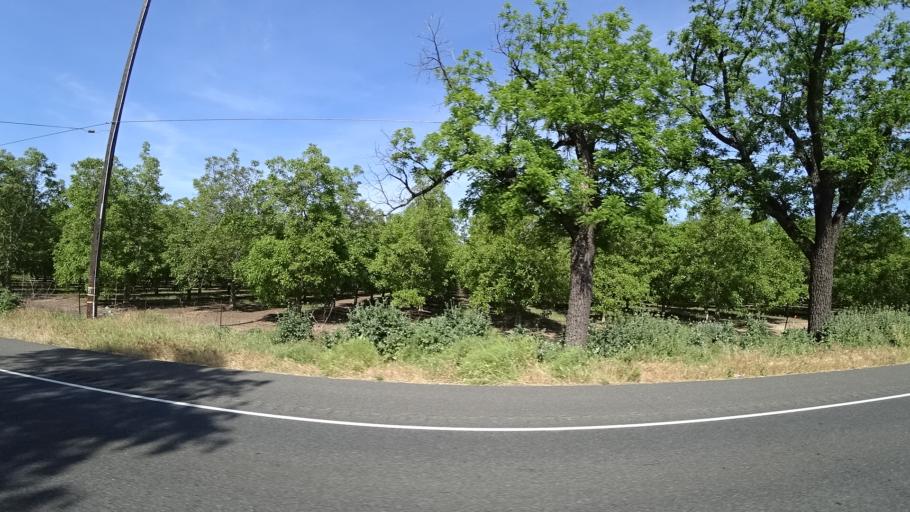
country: US
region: California
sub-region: Tehama County
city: Red Bluff
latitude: 40.1756
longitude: -122.1679
